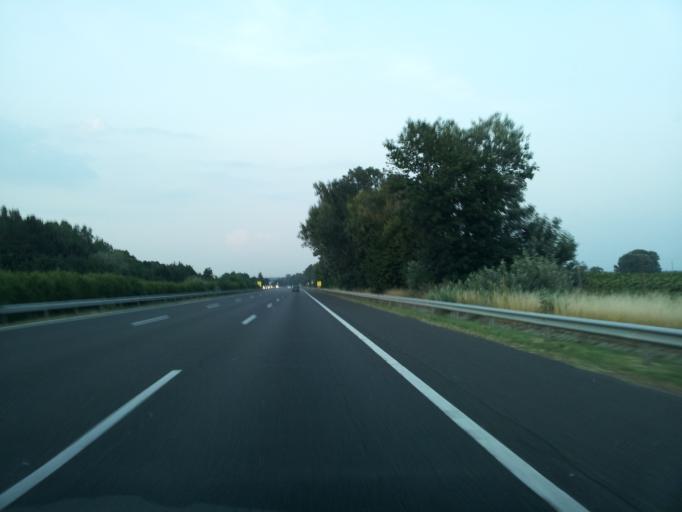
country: HU
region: Fejer
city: Baracska
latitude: 47.2914
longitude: 18.7276
